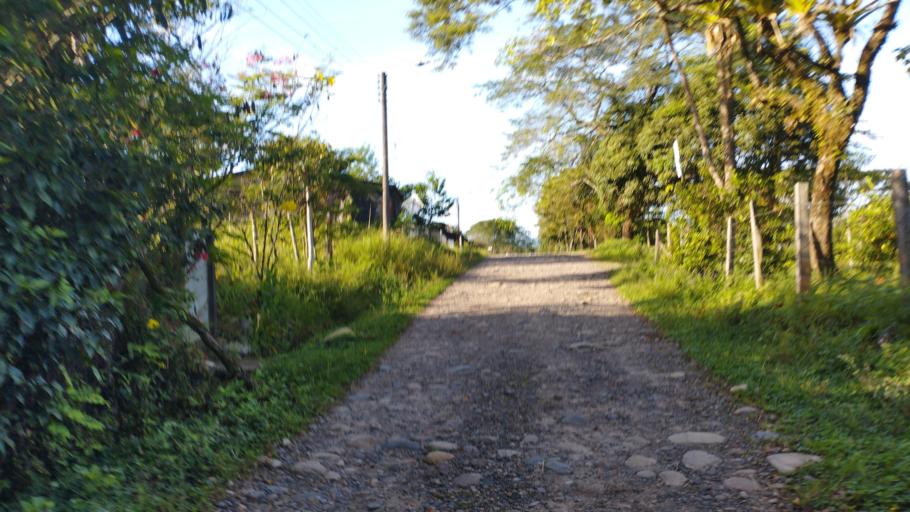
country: CO
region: Casanare
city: Sabanalarga
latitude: 4.8054
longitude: -73.0894
